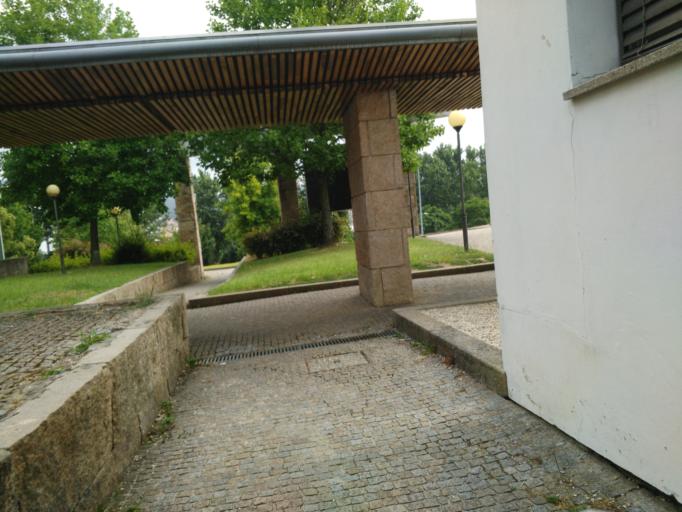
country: PT
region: Braga
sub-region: Braga
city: Braga
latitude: 41.5601
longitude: -8.3972
